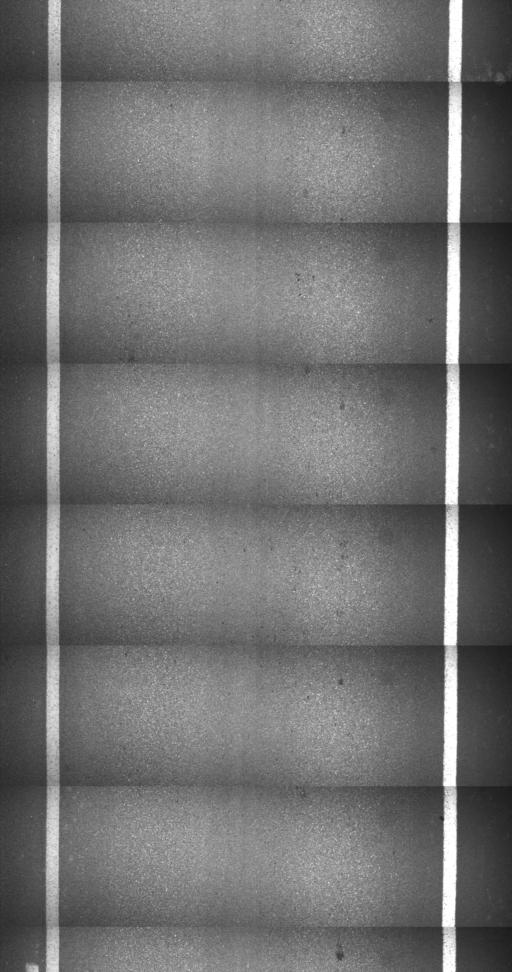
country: US
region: New Hampshire
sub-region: Grafton County
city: Woodsville
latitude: 44.1811
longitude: -72.0612
